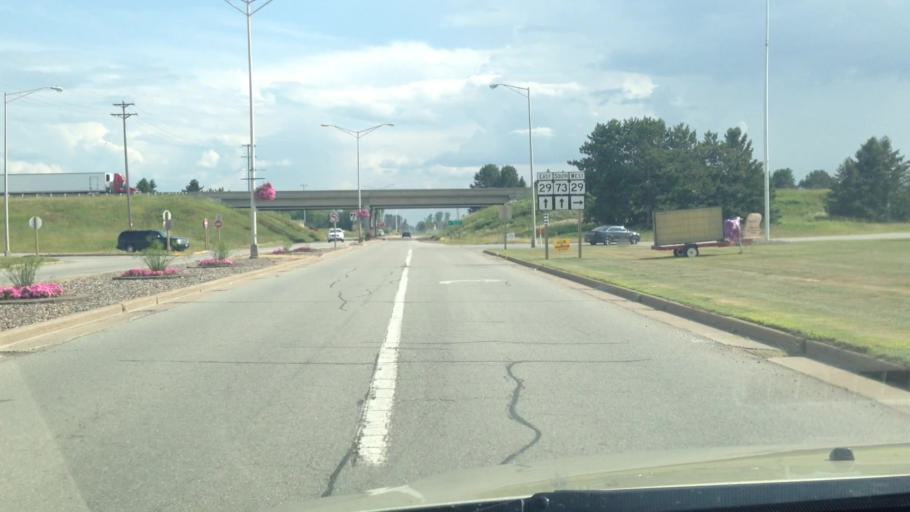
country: US
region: Wisconsin
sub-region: Clark County
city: Thorp
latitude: 44.9530
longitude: -90.8004
